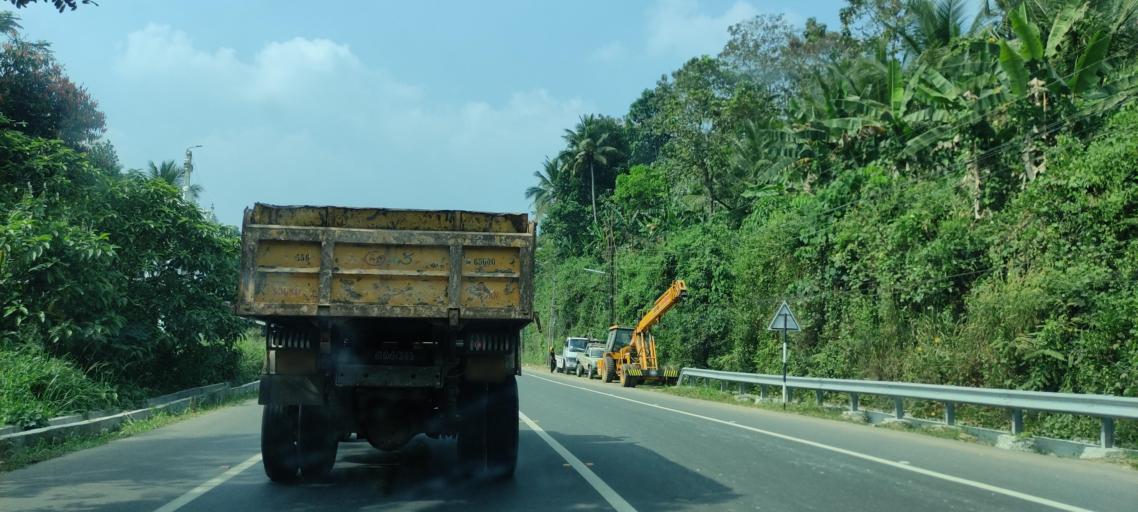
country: IN
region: Kerala
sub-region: Pattanamtitta
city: Adur
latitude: 9.1659
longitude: 76.7188
